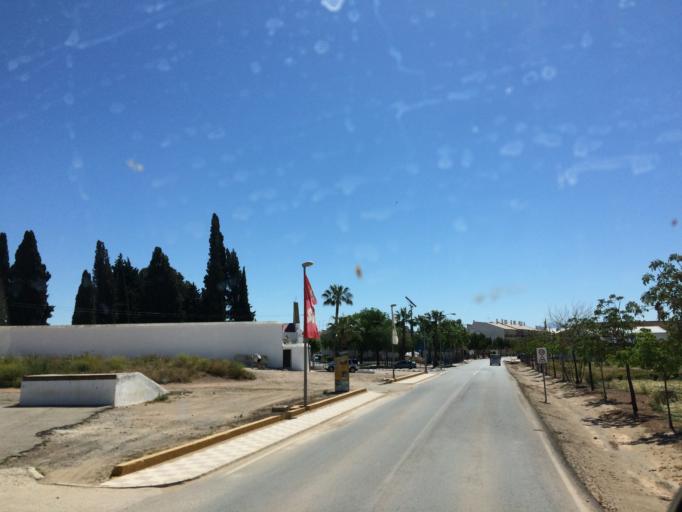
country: ES
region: Andalusia
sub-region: Provincia de Malaga
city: Campillos
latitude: 37.0490
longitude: -4.8701
